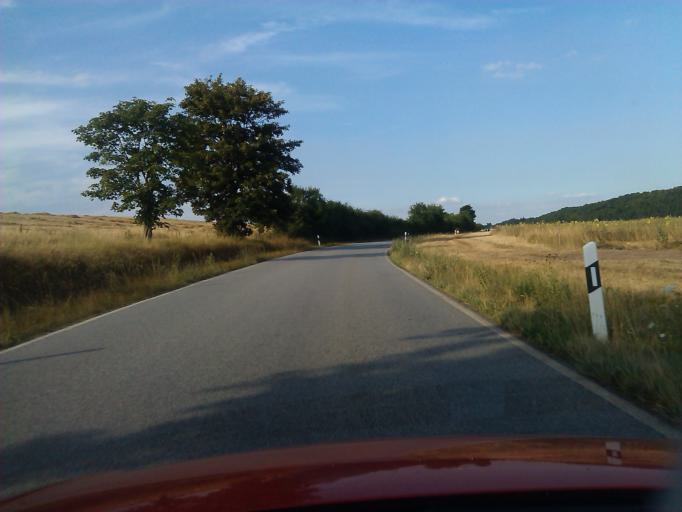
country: DE
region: Baden-Wuerttemberg
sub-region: Regierungsbezirk Stuttgart
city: Zaberfeld
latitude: 49.0649
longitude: 8.9334
